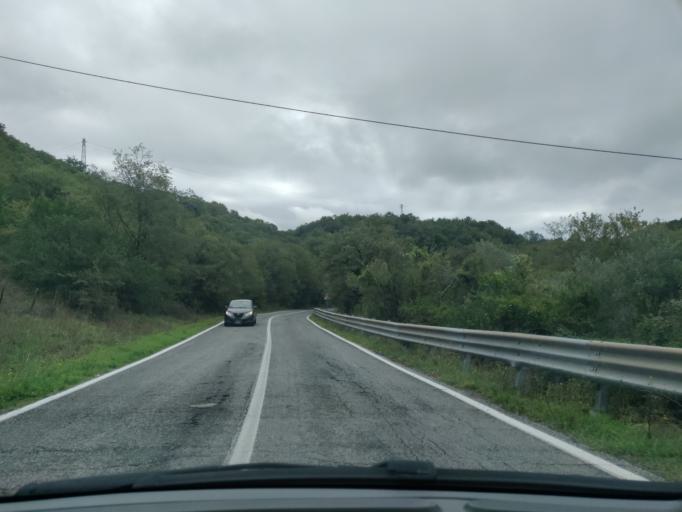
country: IT
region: Latium
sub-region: Citta metropolitana di Roma Capitale
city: Allumiere
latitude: 42.1473
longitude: 11.8958
